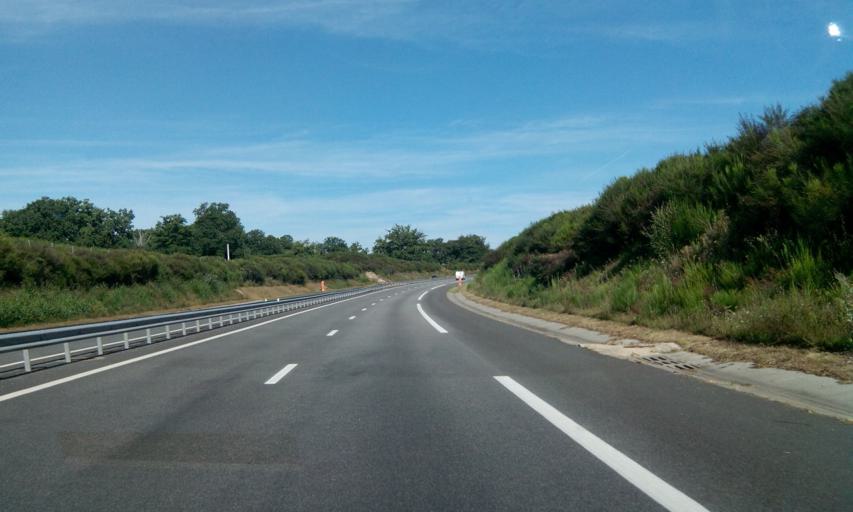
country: FR
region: Limousin
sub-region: Departement de la Haute-Vienne
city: Veyrac
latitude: 45.8769
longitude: 1.1075
